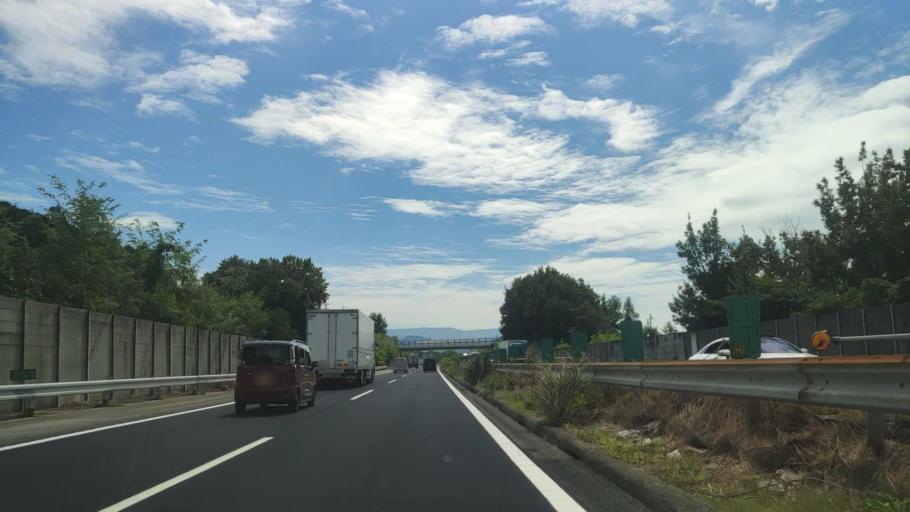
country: JP
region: Aichi
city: Okazaki
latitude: 34.9498
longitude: 137.1971
